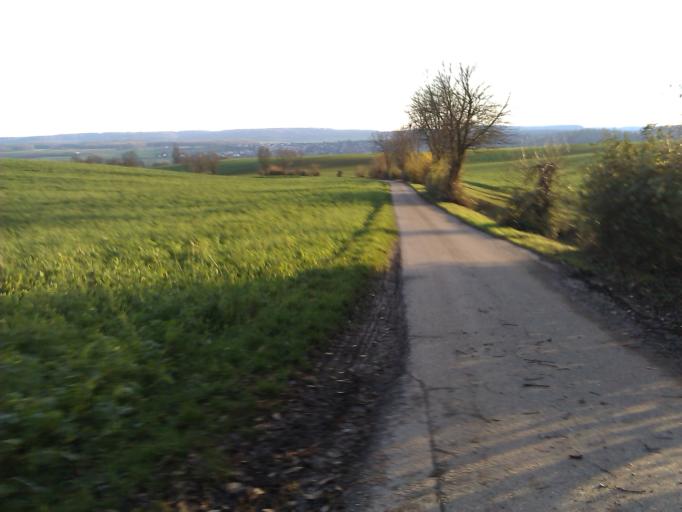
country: DE
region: Baden-Wuerttemberg
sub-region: Regierungsbezirk Stuttgart
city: Oedheim
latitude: 49.2638
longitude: 9.2509
